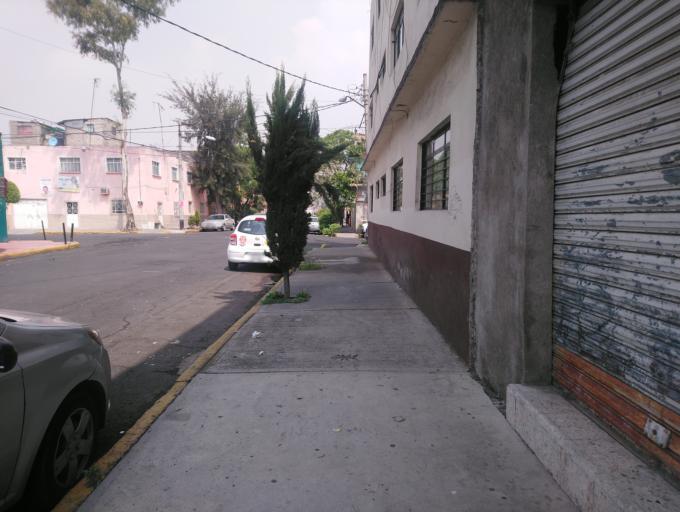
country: MX
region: Mexico City
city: Gustavo A. Madero
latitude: 19.4708
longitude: -99.1031
